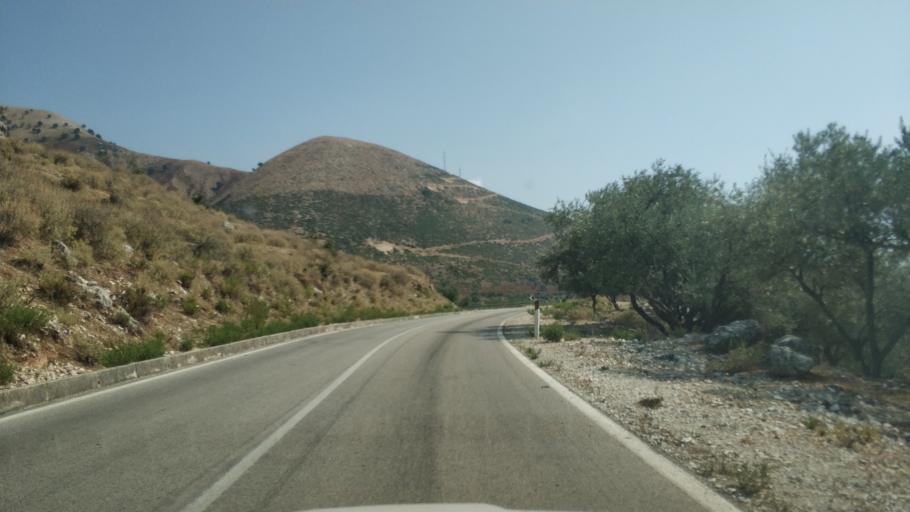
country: AL
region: Vlore
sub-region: Rrethi i Sarandes
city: Lukove
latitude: 40.0358
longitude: 19.8828
